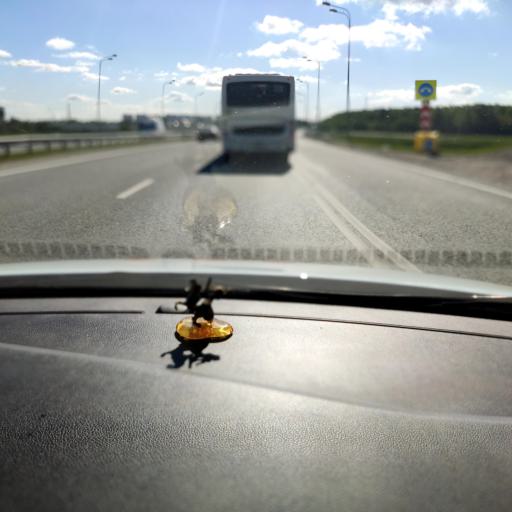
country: RU
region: Tatarstan
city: Osinovo
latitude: 55.8583
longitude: 48.8489
